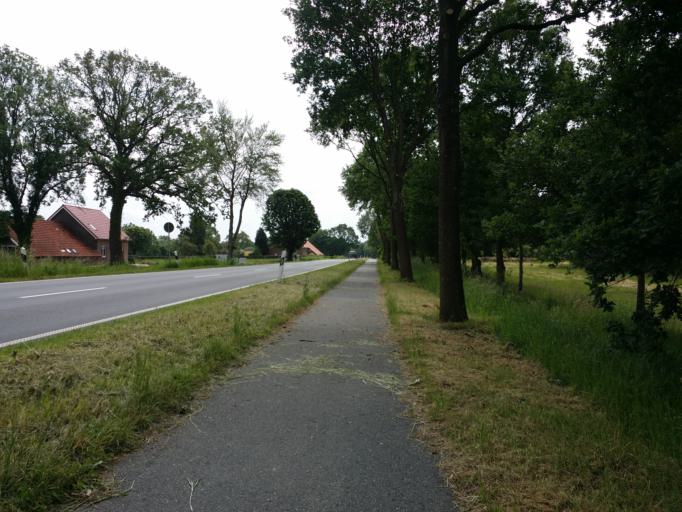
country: DE
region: Lower Saxony
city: Friedeburg
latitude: 53.4297
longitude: 7.8598
